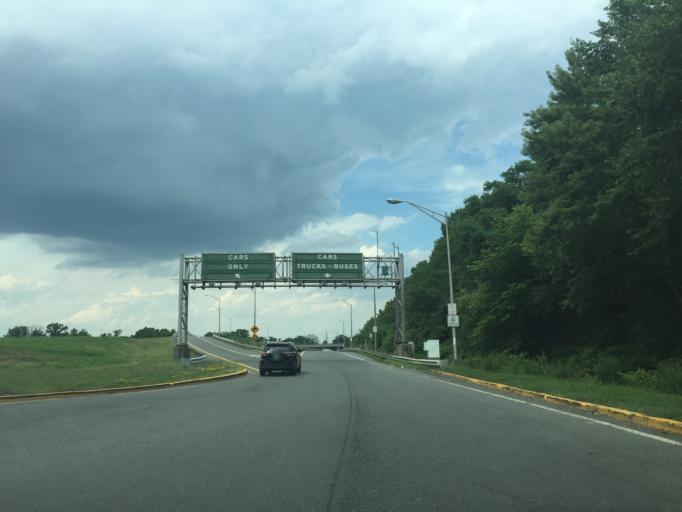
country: US
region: New Jersey
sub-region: Middlesex County
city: Sewaren
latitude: 40.5584
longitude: -74.2616
